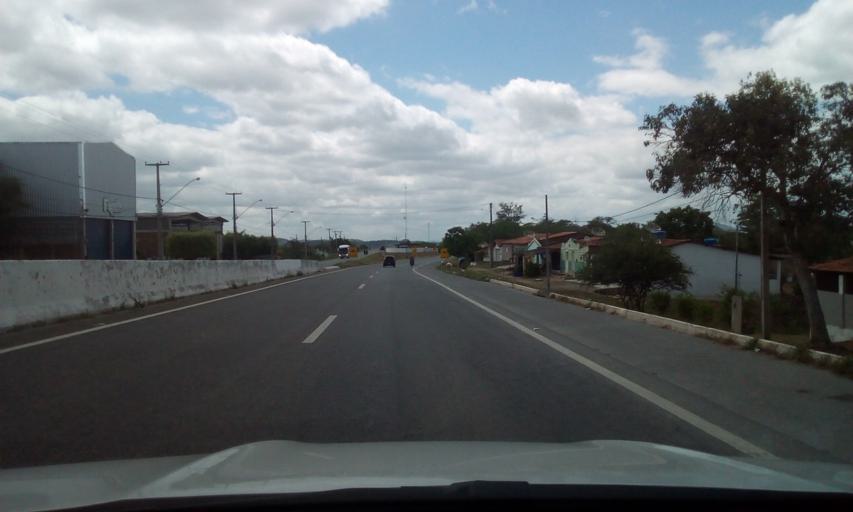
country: BR
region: Paraiba
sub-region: Campina Grande
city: Campina Grande
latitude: -7.2531
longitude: -35.8340
